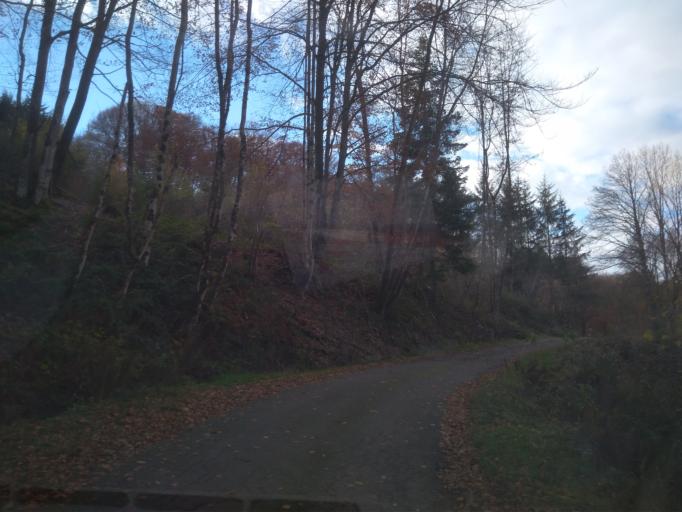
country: FR
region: Rhone-Alpes
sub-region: Departement de la Loire
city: La Pacaudiere
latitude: 46.1294
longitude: 3.7891
